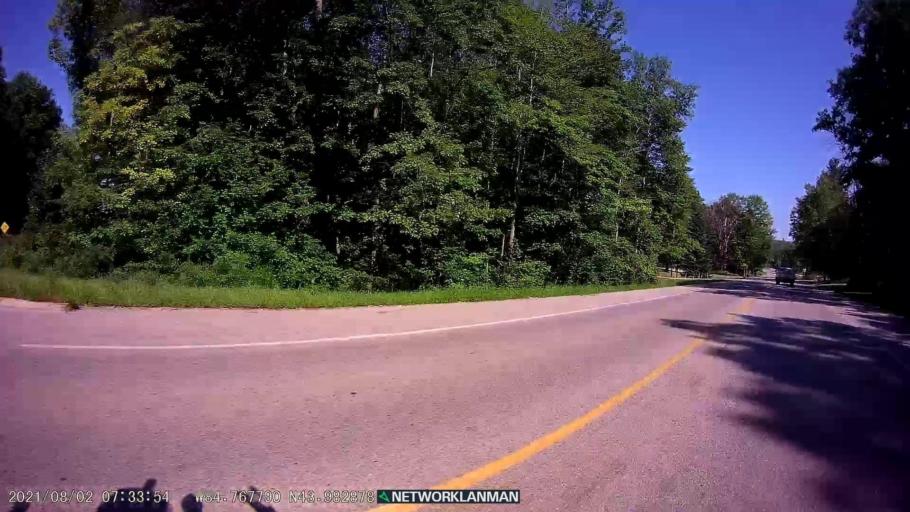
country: US
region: Michigan
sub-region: Clare County
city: Harrison
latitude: 43.9829
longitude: -84.7678
